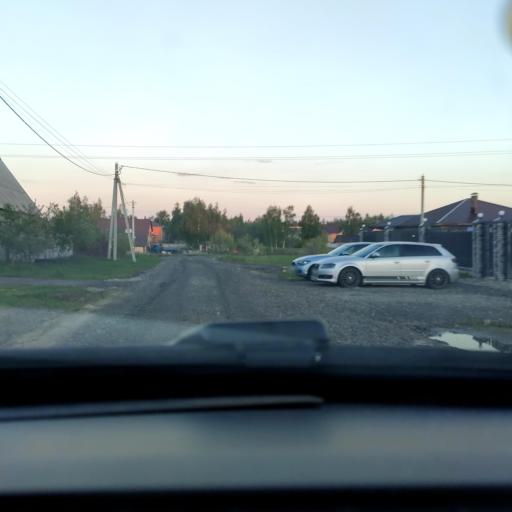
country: RU
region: Voronezj
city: Novaya Usman'
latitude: 51.6555
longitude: 39.4232
